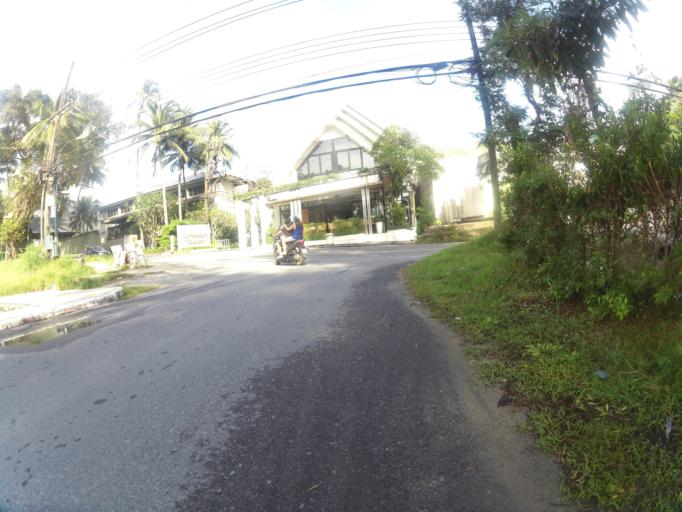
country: TH
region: Phuket
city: Thalang
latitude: 7.9767
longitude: 98.2802
